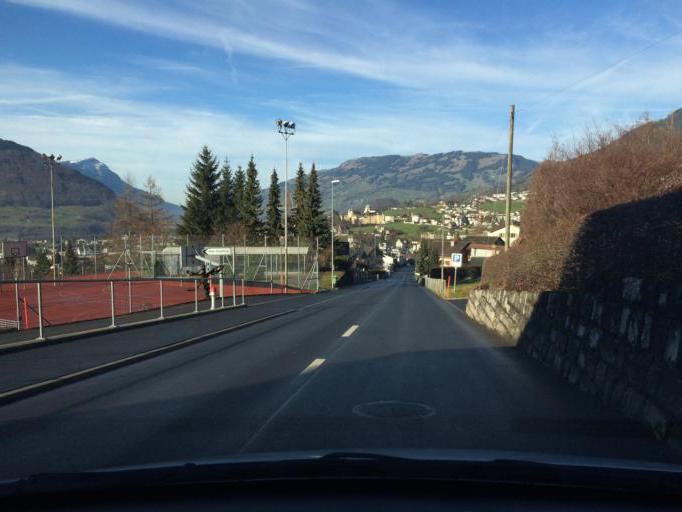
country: CH
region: Schwyz
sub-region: Bezirk Schwyz
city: Schwyz
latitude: 47.0165
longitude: 8.6660
